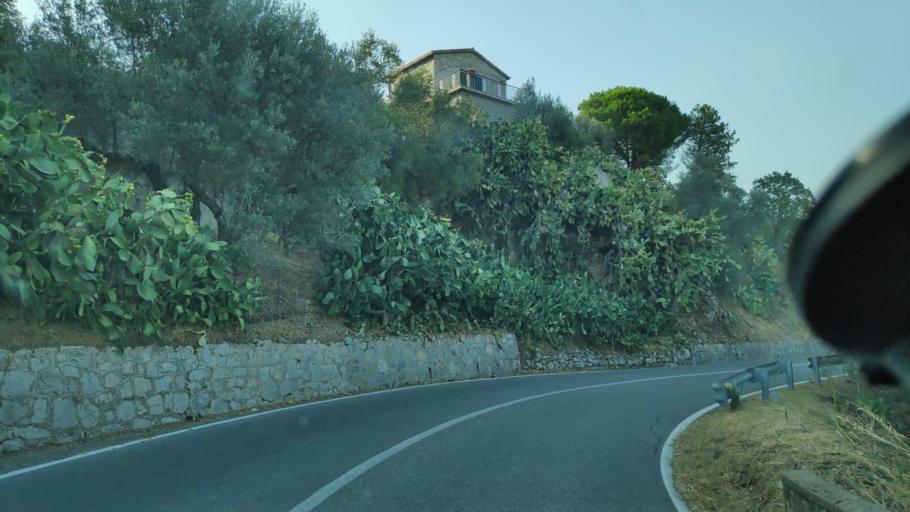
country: IT
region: Calabria
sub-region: Provincia di Catanzaro
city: Sant'Andrea Apostolo dello Ionio
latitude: 38.6216
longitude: 16.5382
